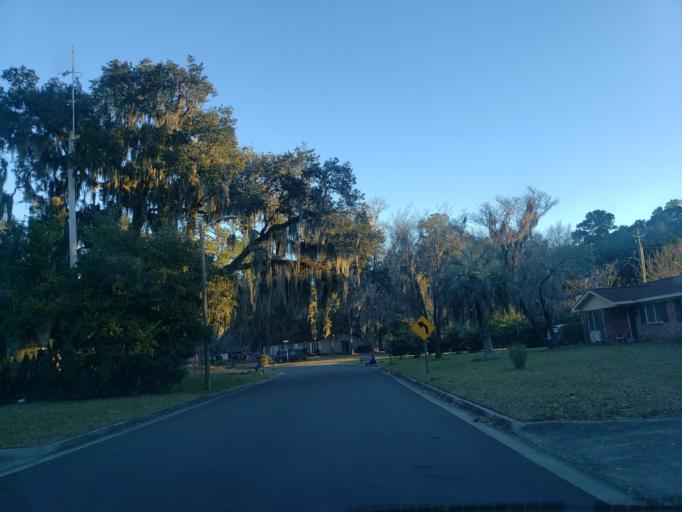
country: US
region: Georgia
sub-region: Chatham County
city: Isle of Hope
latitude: 31.9773
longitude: -81.1001
